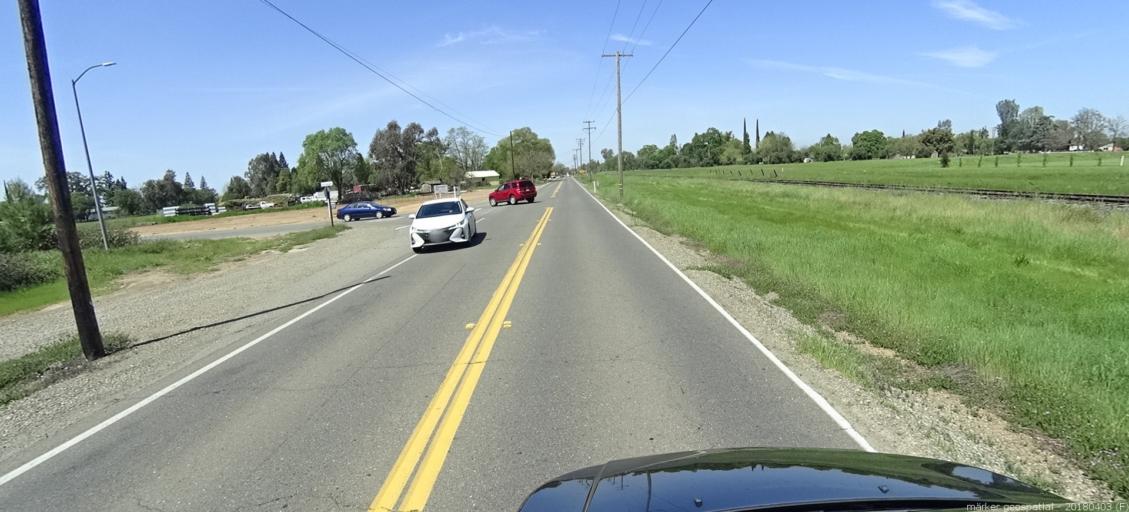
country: US
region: California
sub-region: Sacramento County
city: Wilton
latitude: 38.4096
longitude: -121.2692
